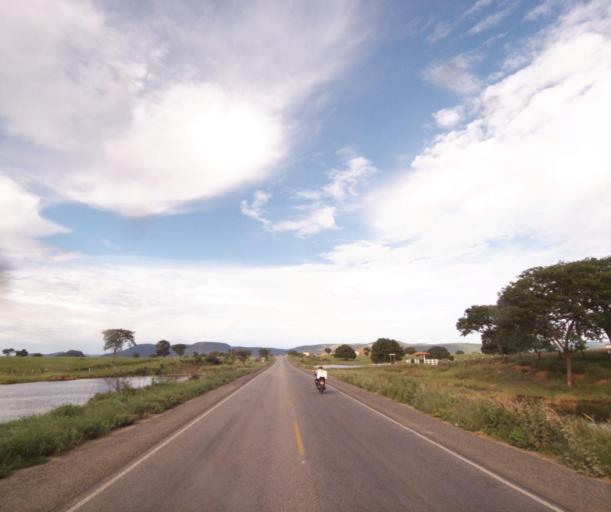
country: BR
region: Bahia
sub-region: Guanambi
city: Guanambi
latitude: -14.1957
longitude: -42.7494
